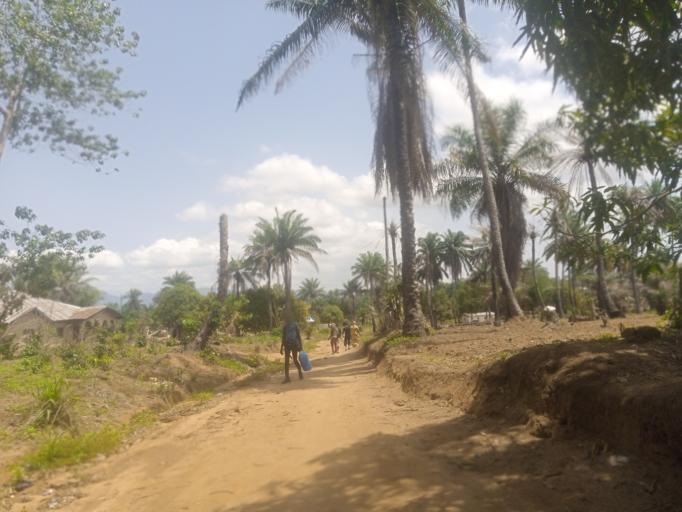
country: SL
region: Western Area
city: Waterloo
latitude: 8.3186
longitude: -13.0072
